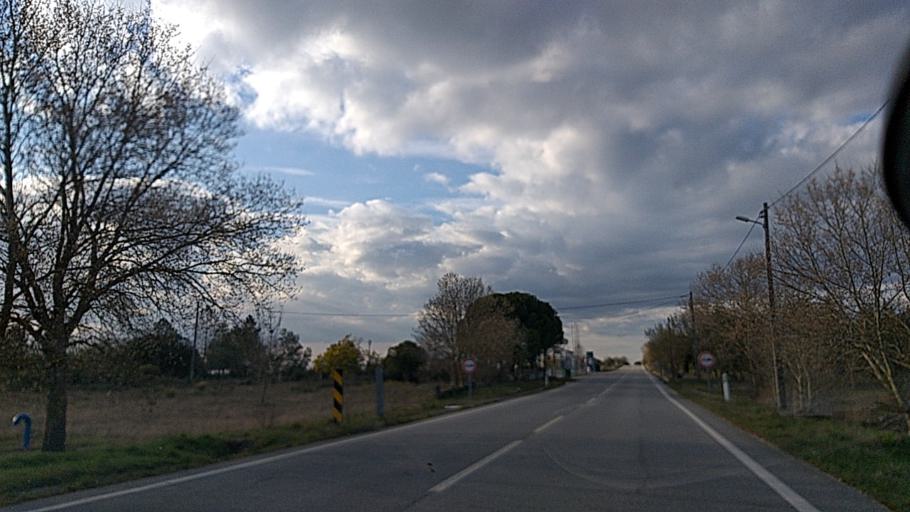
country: ES
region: Castille and Leon
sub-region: Provincia de Salamanca
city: Aldea del Obispo
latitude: 40.7010
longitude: -6.8914
